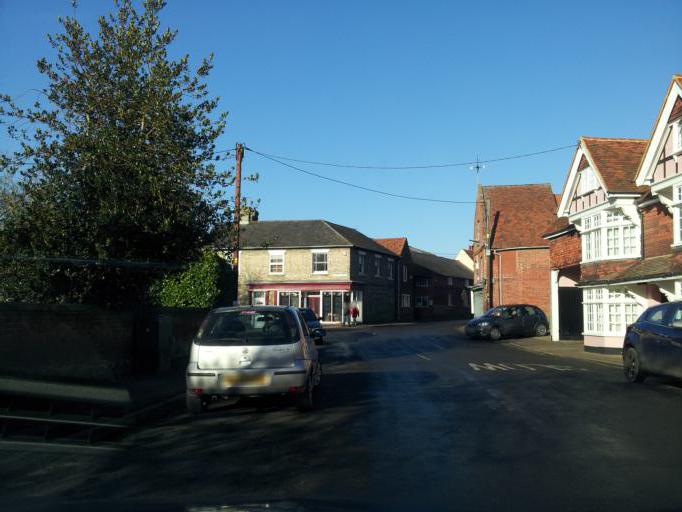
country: GB
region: England
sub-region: Suffolk
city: Sudbury
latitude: 51.9720
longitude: 0.7753
